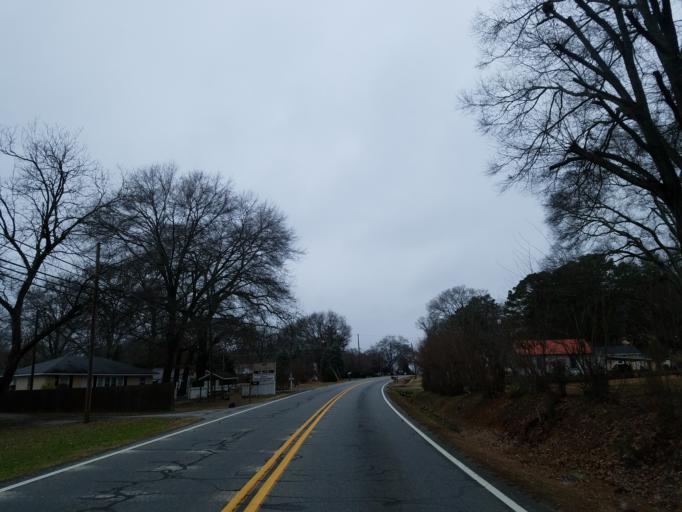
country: US
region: Georgia
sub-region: Bartow County
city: Cartersville
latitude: 34.1916
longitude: -84.8212
